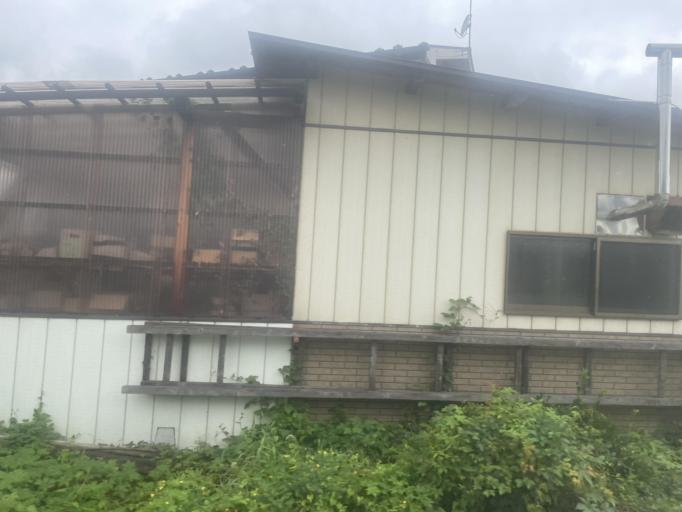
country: JP
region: Saitama
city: Chichibu
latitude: 35.9571
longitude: 139.0327
